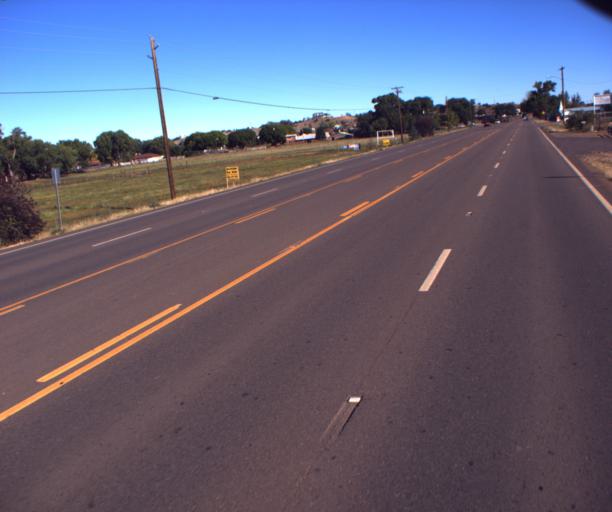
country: US
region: Arizona
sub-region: Navajo County
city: Taylor
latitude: 34.4831
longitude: -110.0835
